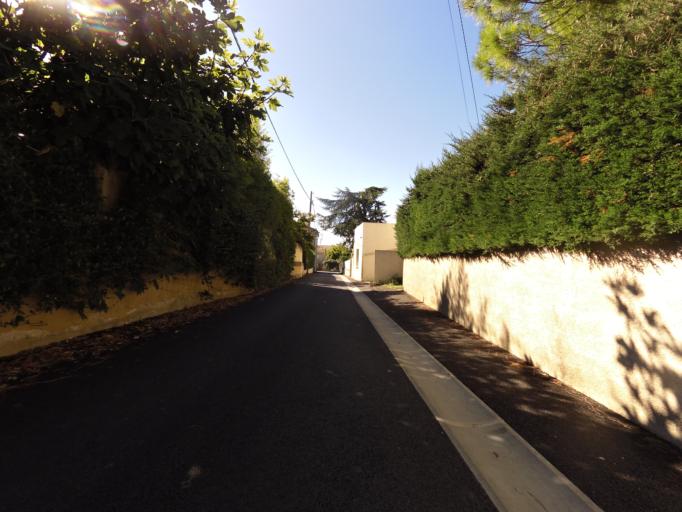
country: FR
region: Languedoc-Roussillon
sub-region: Departement du Gard
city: Aigues-Vives
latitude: 43.7420
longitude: 4.1709
